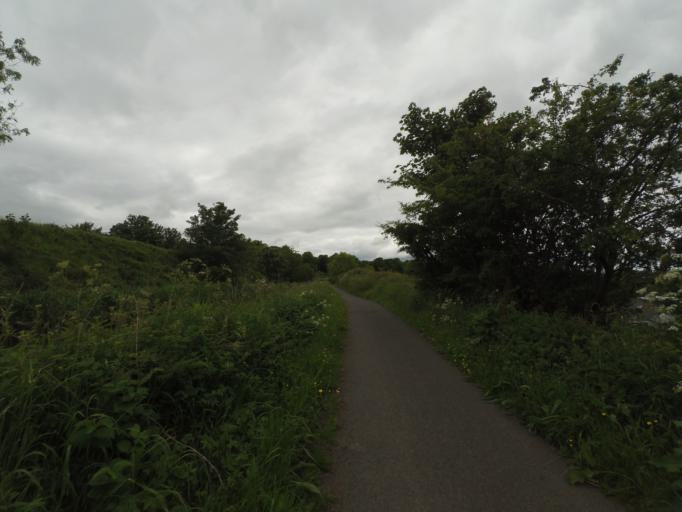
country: GB
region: Scotland
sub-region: West Lothian
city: Linlithgow
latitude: 55.9767
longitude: -3.5834
